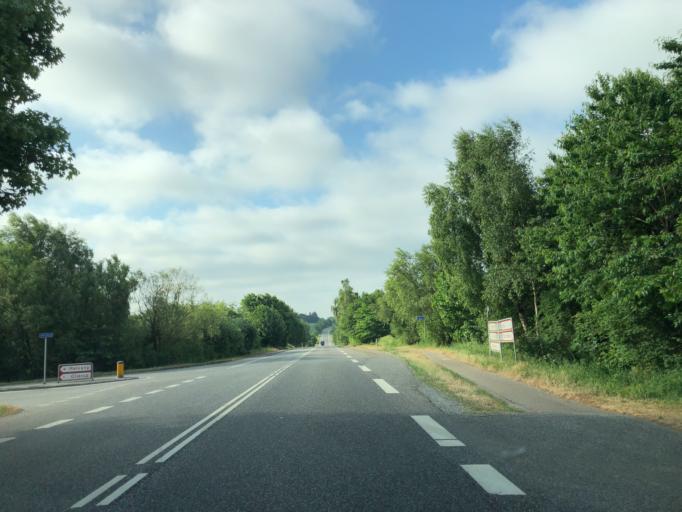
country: DK
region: South Denmark
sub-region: Vejle Kommune
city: Jelling
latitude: 55.7232
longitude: 9.3656
